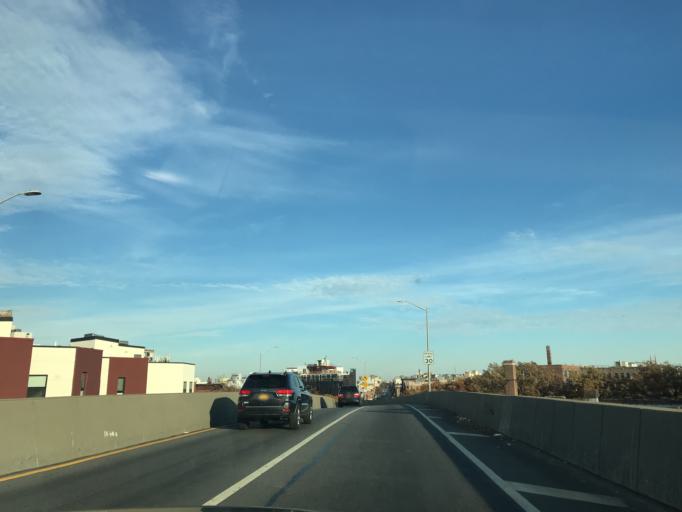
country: US
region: New York
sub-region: Queens County
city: Long Island City
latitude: 40.7102
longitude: -73.9581
